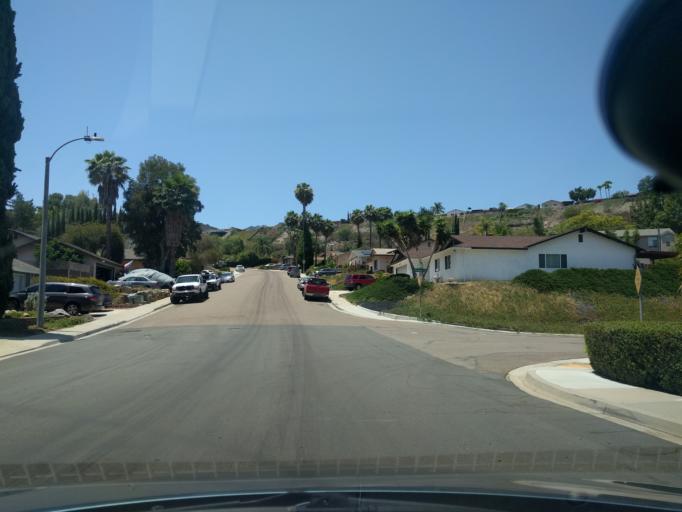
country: US
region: California
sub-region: San Diego County
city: Poway
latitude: 32.9959
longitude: -117.0911
